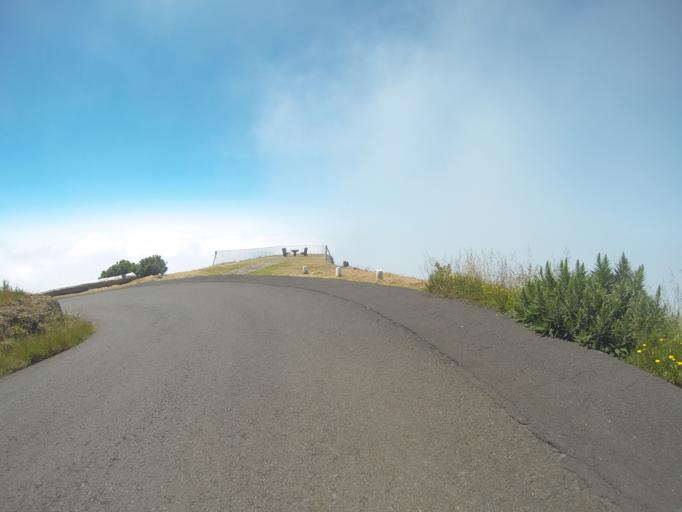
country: PT
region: Madeira
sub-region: Funchal
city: Nossa Senhora do Monte
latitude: 32.7004
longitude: -16.9149
